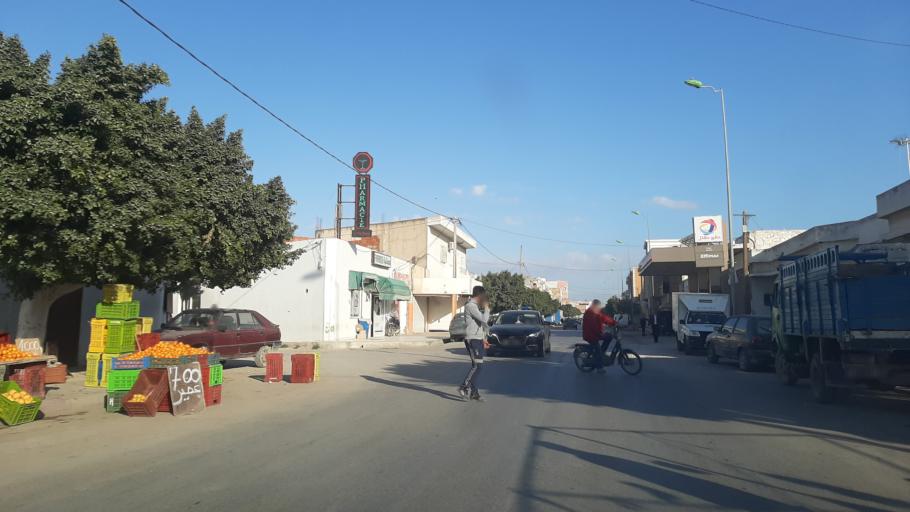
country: TN
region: Al Mahdiyah
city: El Jem
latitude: 35.2977
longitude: 10.7081
